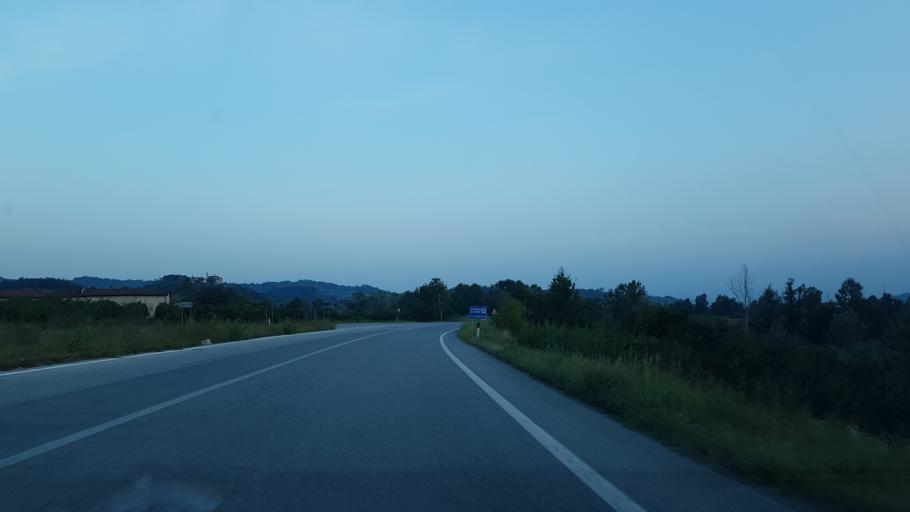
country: IT
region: Piedmont
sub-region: Provincia di Cuneo
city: Monchiero Borgonuovo
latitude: 44.5806
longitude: 7.9087
